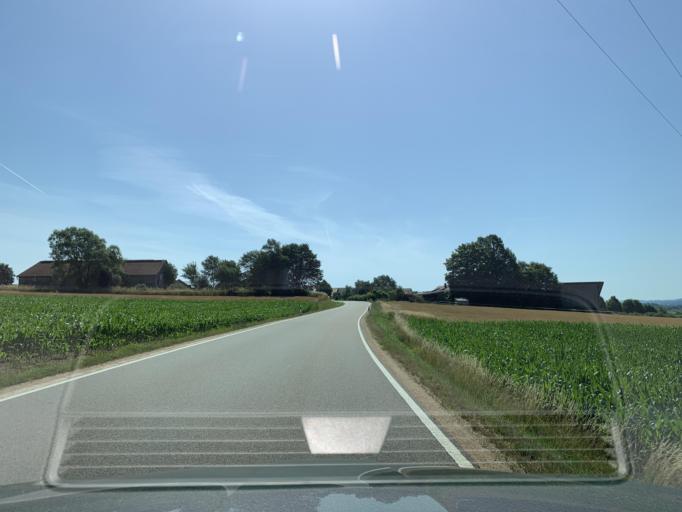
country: DE
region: Bavaria
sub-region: Upper Palatinate
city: Schwarzhofen
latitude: 49.3961
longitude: 12.3217
